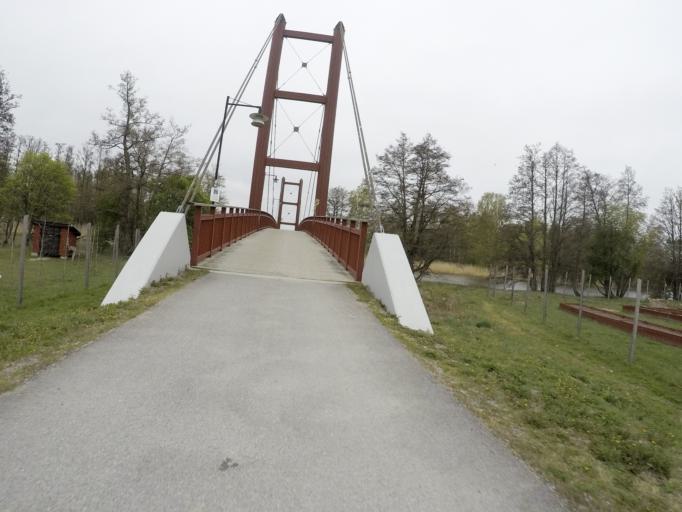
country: SE
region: Soedermanland
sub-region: Eskilstuna Kommun
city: Torshalla
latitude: 59.3837
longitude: 16.4758
